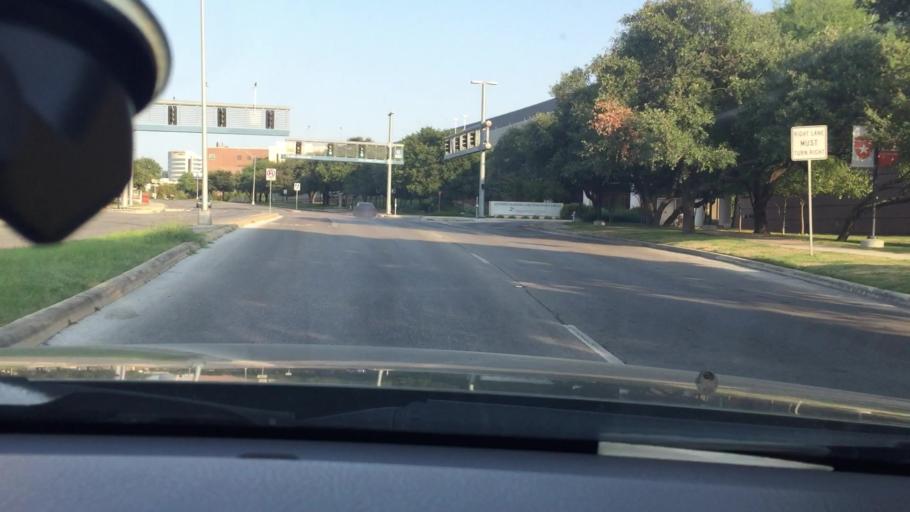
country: US
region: Texas
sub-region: Bexar County
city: Leon Valley
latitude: 29.5152
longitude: -98.5839
